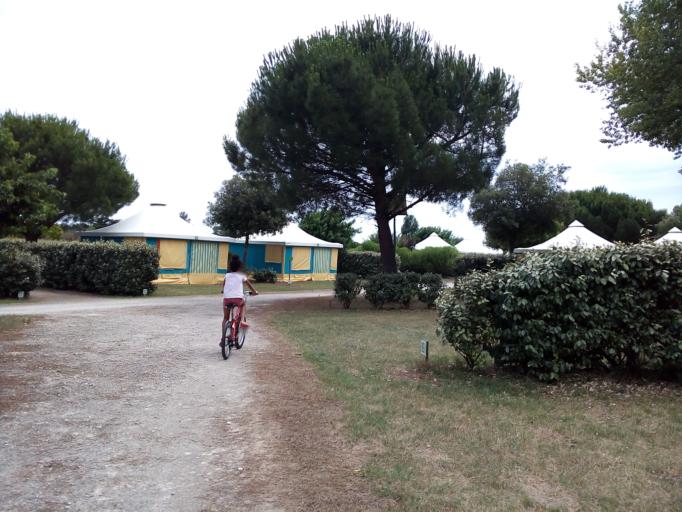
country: FR
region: Poitou-Charentes
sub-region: Departement de la Charente-Maritime
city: Boyard-Ville
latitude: 45.9501
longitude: -1.2493
